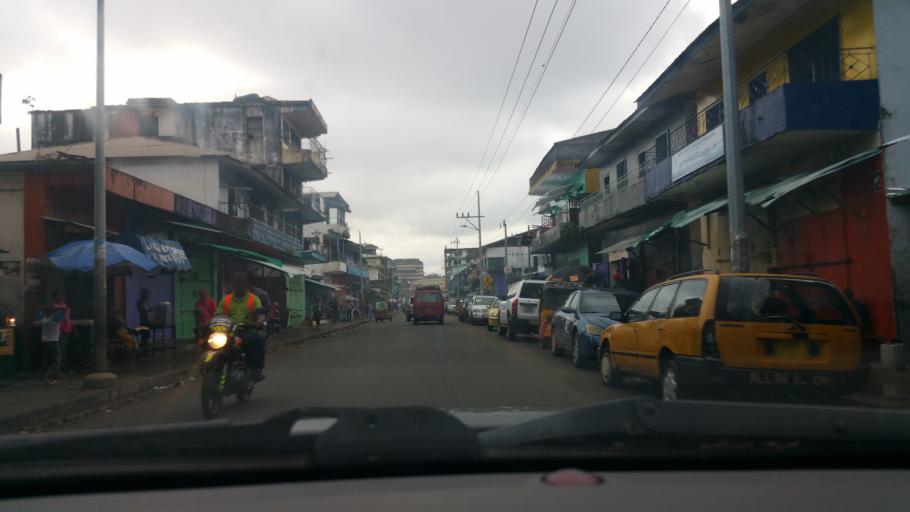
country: LR
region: Montserrado
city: Monrovia
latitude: 6.3089
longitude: -10.8000
